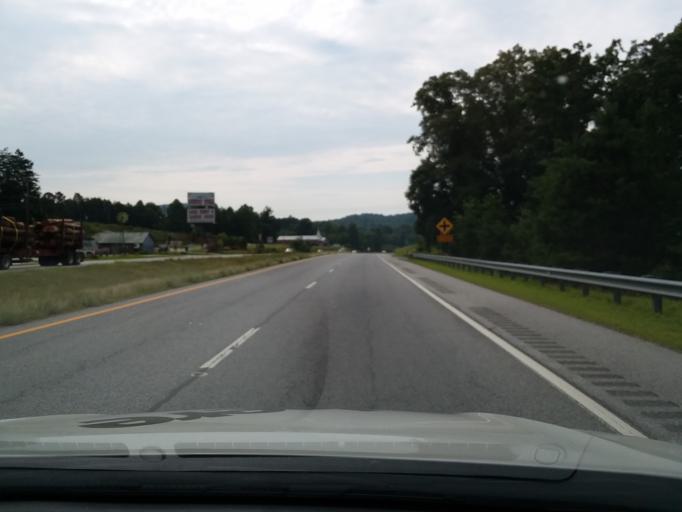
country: US
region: Georgia
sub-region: Rabun County
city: Clayton
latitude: 34.8003
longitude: -83.4231
